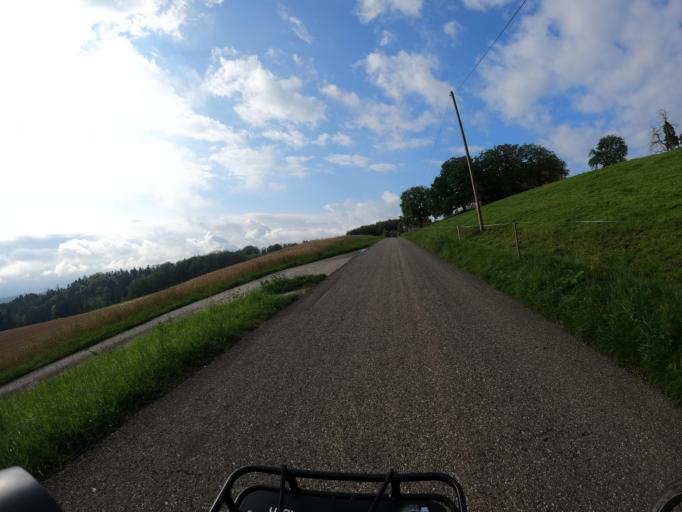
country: CH
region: Aargau
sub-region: Bezirk Muri
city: Buttwil
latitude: 47.2403
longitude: 8.3259
